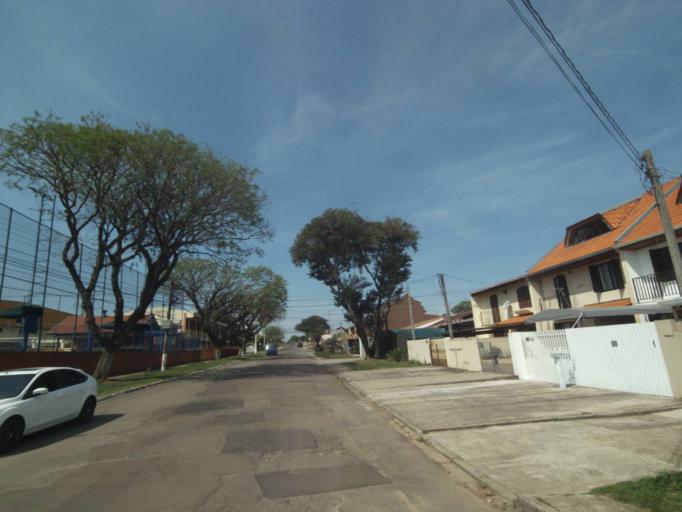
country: BR
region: Parana
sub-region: Curitiba
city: Curitiba
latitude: -25.4641
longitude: -49.3125
